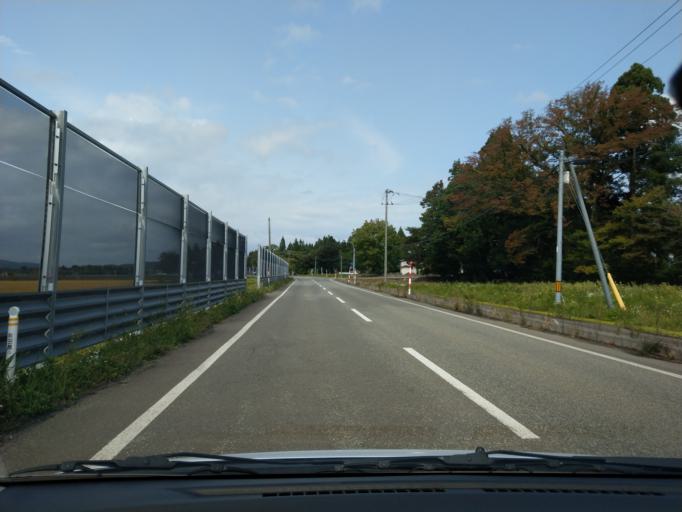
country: JP
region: Akita
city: Omagari
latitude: 39.5268
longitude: 140.2635
